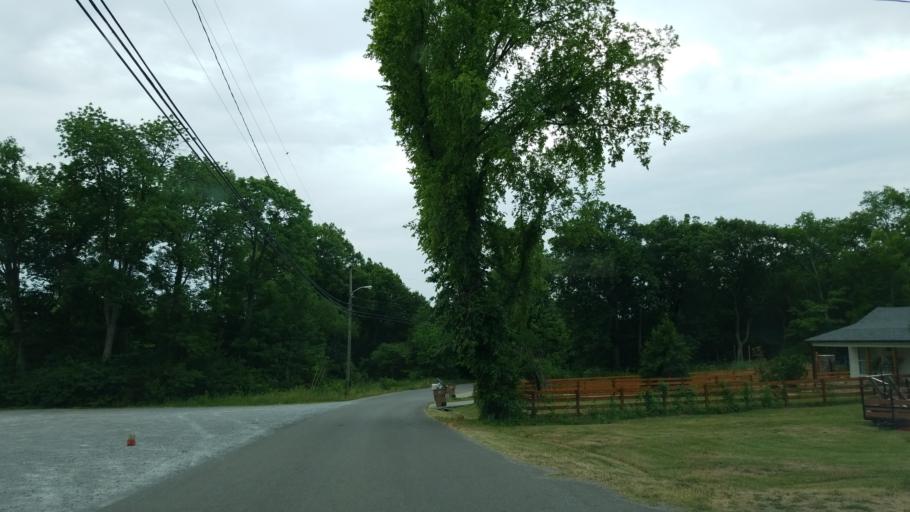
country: US
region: Tennessee
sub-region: Rutherford County
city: La Vergne
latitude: 36.0358
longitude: -86.6042
